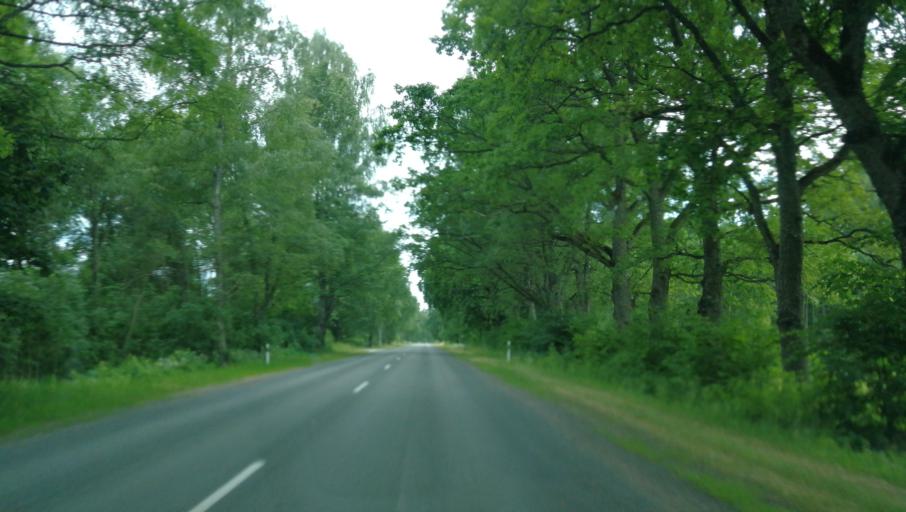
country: LV
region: Valmieras Rajons
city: Valmiera
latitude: 57.6635
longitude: 25.4290
